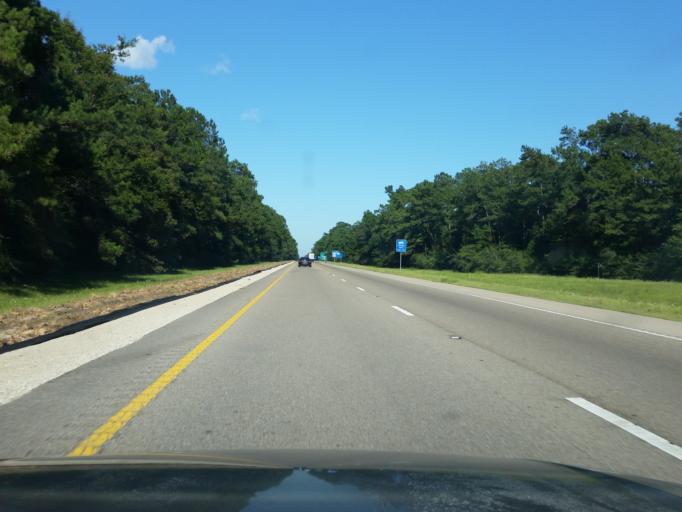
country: US
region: Mississippi
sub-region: Hancock County
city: Pearlington
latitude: 30.3076
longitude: -89.6236
